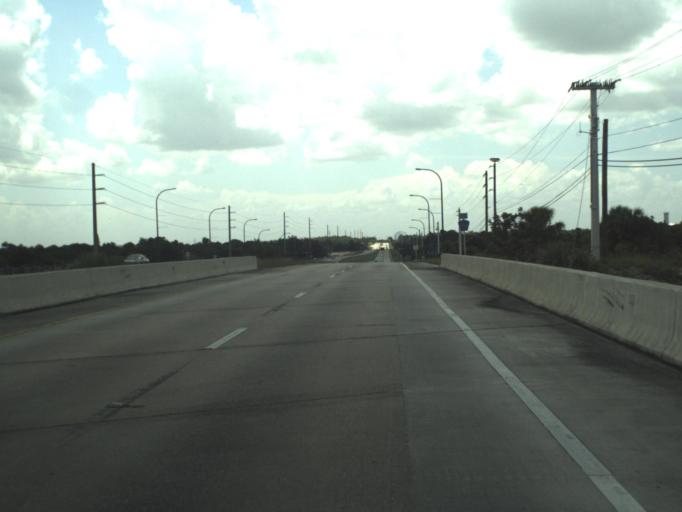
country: US
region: Florida
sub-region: Martin County
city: Hobe Sound
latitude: 27.0442
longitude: -80.1171
